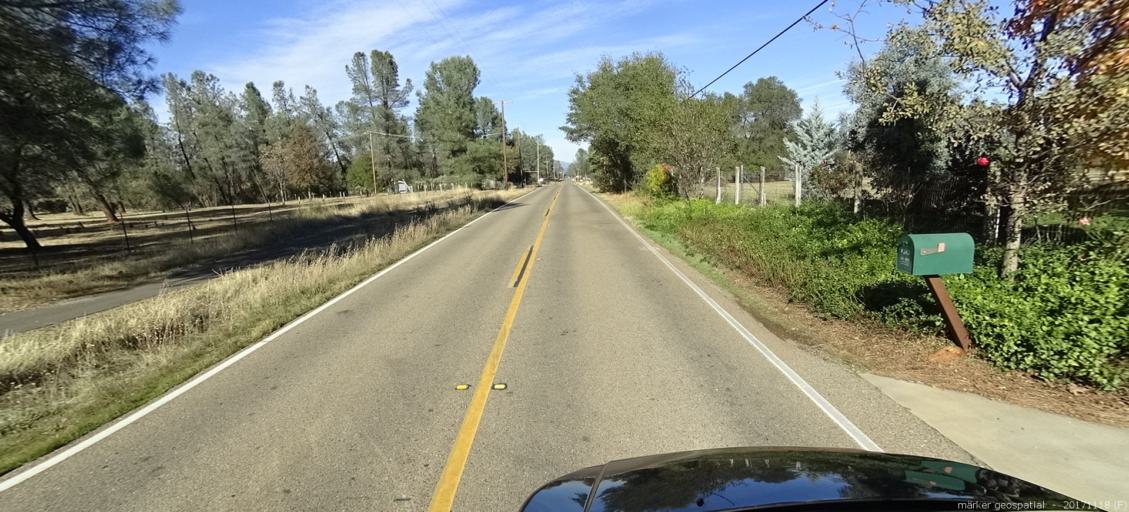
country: US
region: California
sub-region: Shasta County
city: Redding
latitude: 40.4603
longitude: -122.4546
